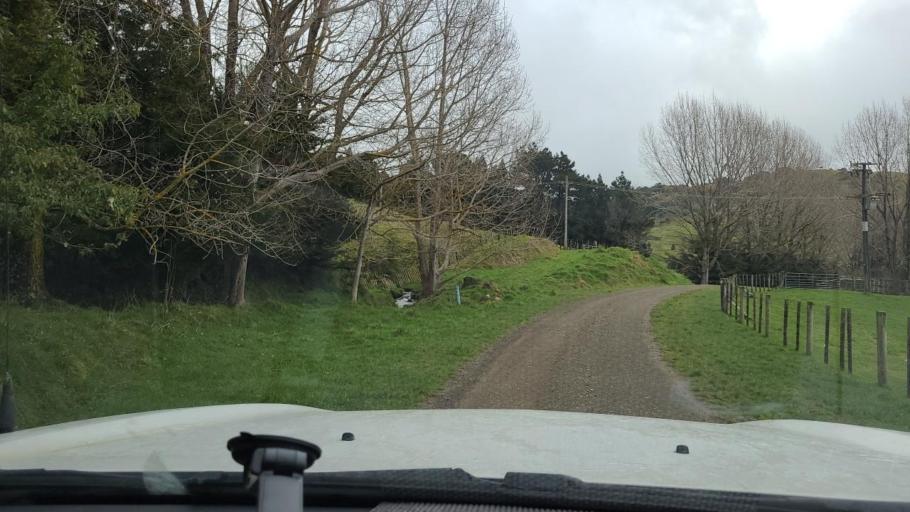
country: NZ
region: Hawke's Bay
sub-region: Wairoa District
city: Wairoa
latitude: -38.5428
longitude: 177.4087
